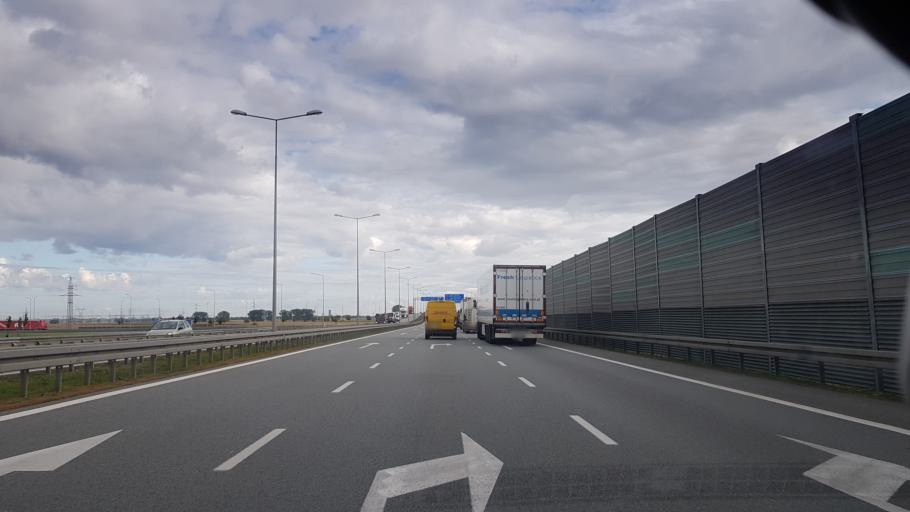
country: PL
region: Greater Poland Voivodeship
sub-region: Powiat poznanski
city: Komorniki
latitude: 52.3481
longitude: 16.7632
